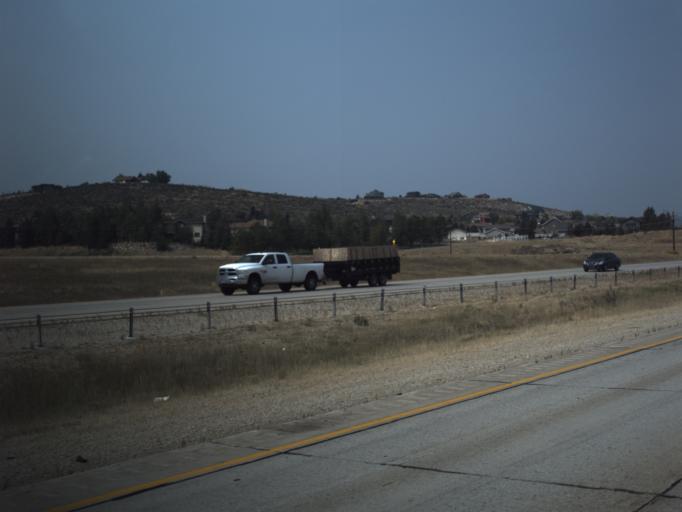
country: US
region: Utah
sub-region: Summit County
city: Snyderville
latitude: 40.7184
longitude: -111.4872
